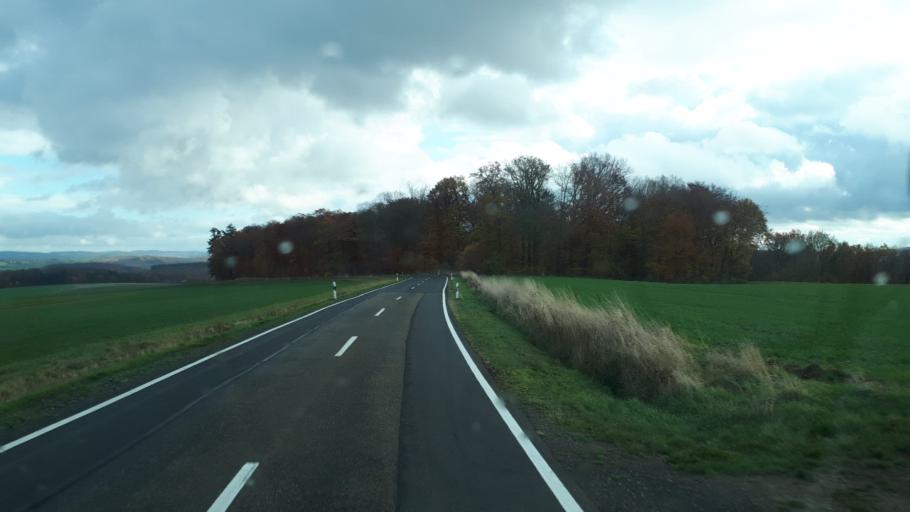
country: DE
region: Rheinland-Pfalz
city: Binningen
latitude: 50.2054
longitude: 7.2610
